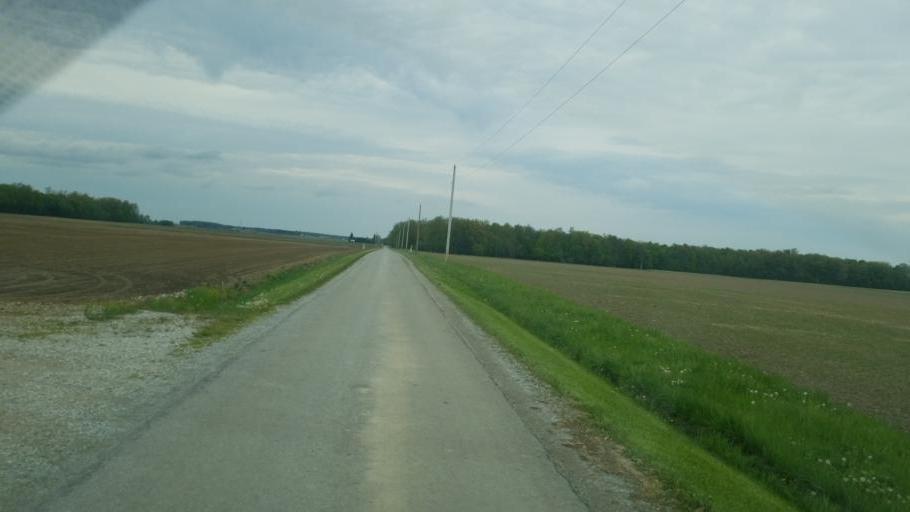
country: US
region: Ohio
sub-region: Huron County
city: Willard
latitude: 41.0307
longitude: -82.8619
